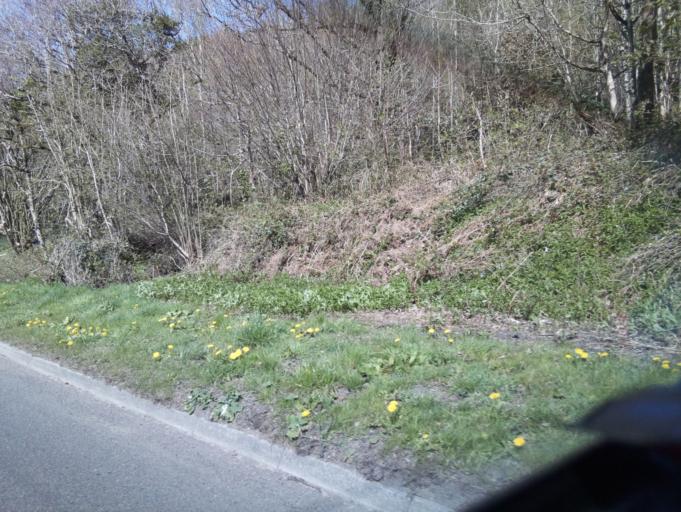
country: GB
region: Wales
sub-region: Rhondda Cynon Taf
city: Mountain Ash
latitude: 51.6715
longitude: -3.3594
